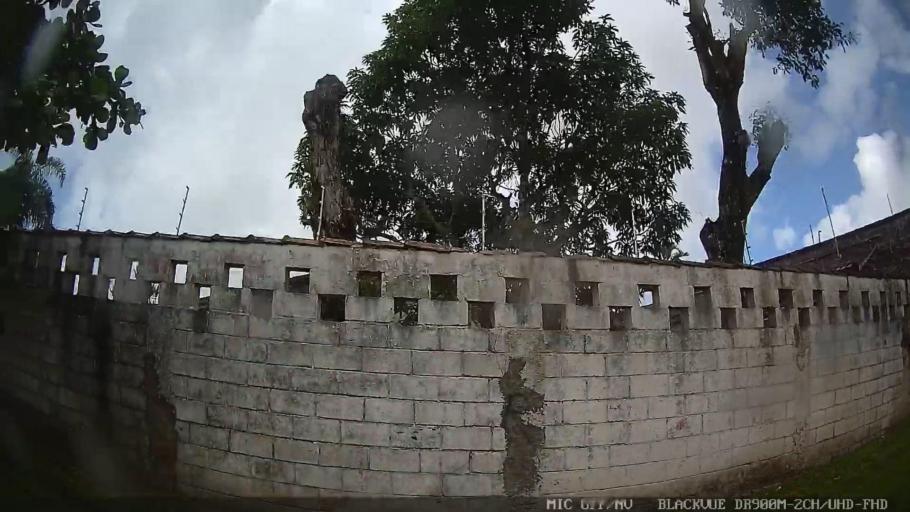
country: BR
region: Sao Paulo
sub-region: Itanhaem
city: Itanhaem
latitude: -24.2172
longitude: -46.8563
